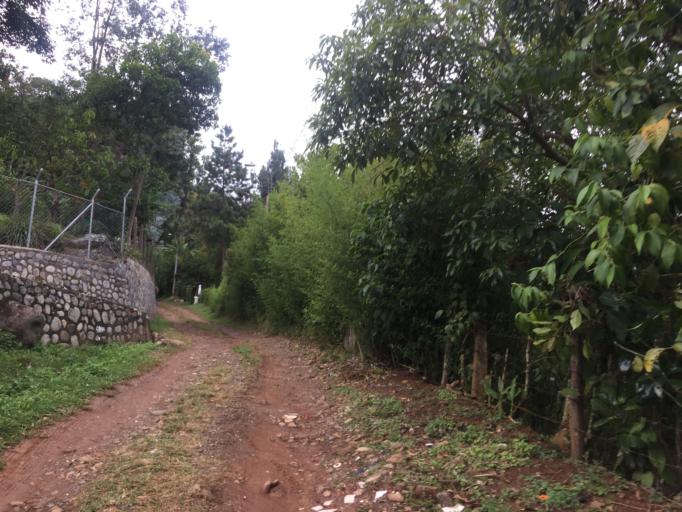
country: CO
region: Valle del Cauca
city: Cali
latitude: 3.4634
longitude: -76.6341
